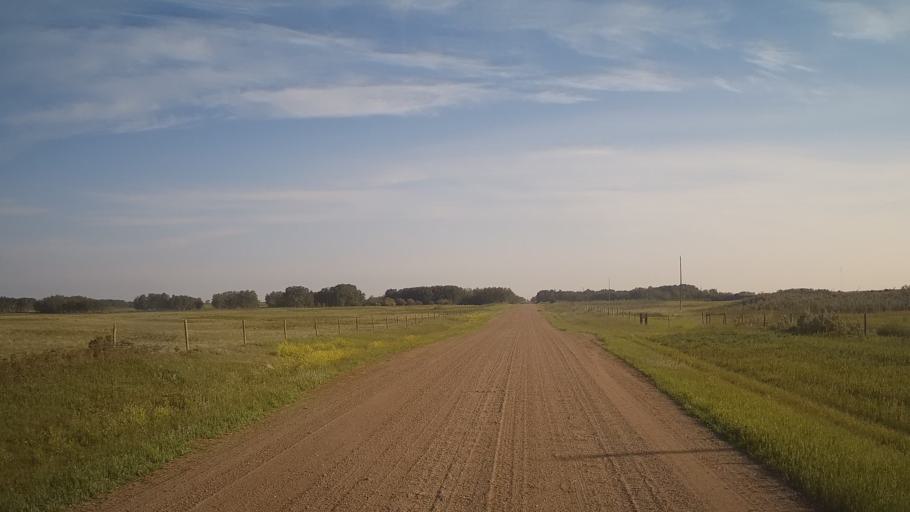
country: CA
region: Saskatchewan
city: Saskatoon
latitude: 51.8250
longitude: -106.5239
